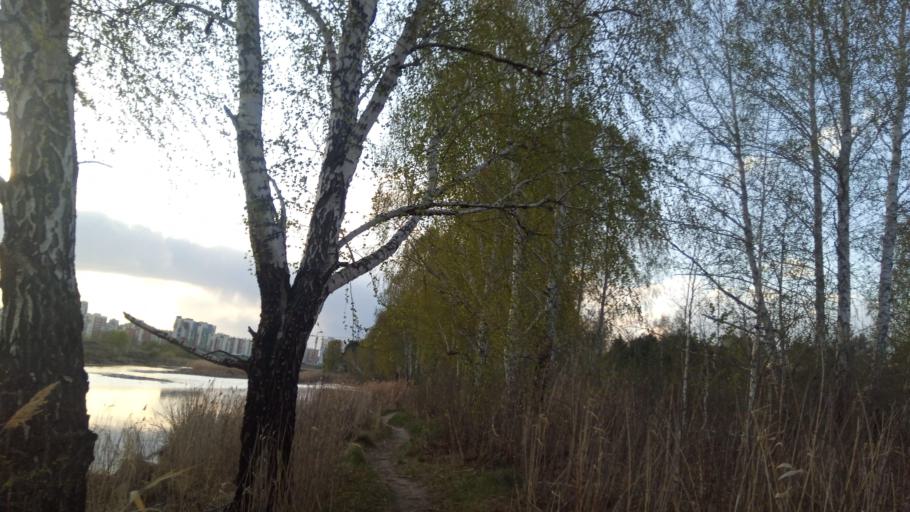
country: RU
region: Chelyabinsk
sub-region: Gorod Chelyabinsk
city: Chelyabinsk
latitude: 55.1588
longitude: 61.3174
